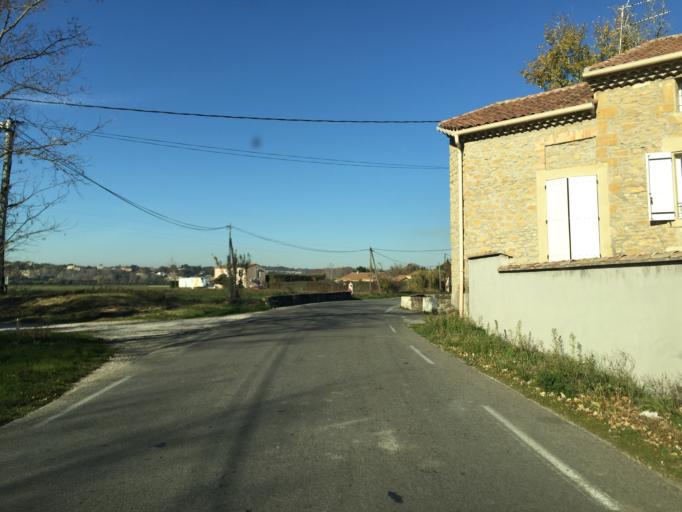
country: FR
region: Provence-Alpes-Cote d'Azur
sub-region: Departement du Vaucluse
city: Bedarrides
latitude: 44.0334
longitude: 4.9122
